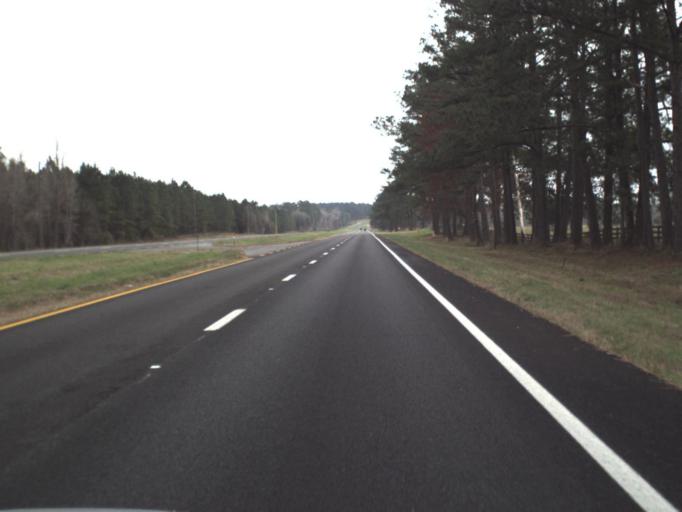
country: US
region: Florida
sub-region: Jefferson County
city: Monticello
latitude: 30.3881
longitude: -83.8500
